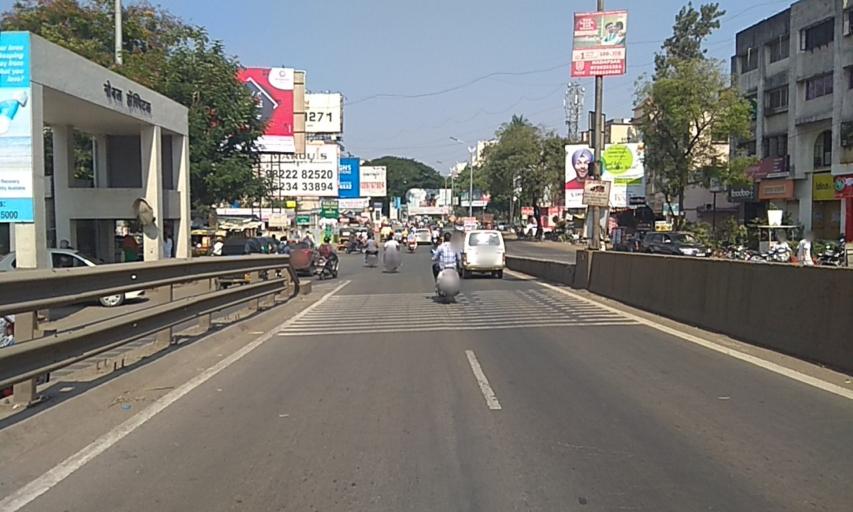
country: IN
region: Maharashtra
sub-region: Pune Division
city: Pune
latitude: 18.5049
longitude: 73.9276
